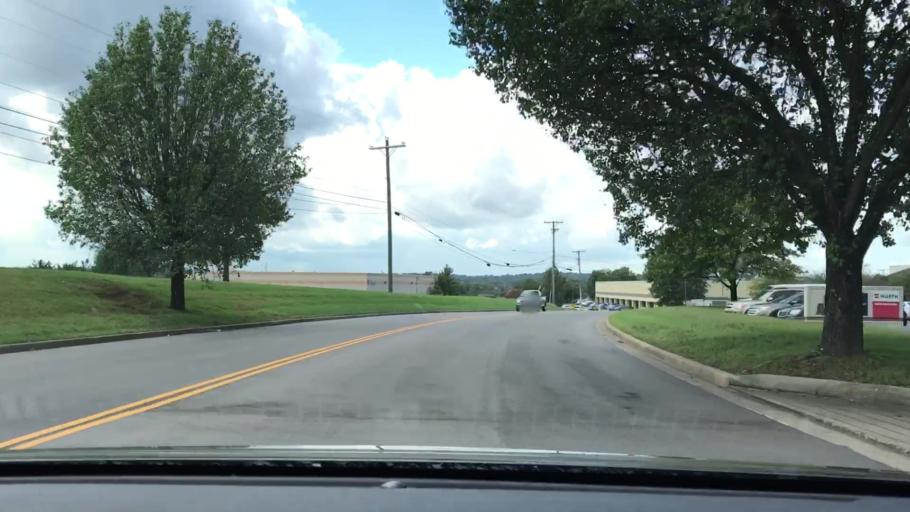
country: US
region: Tennessee
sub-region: Davidson County
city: Oak Hill
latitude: 36.1188
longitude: -86.7571
